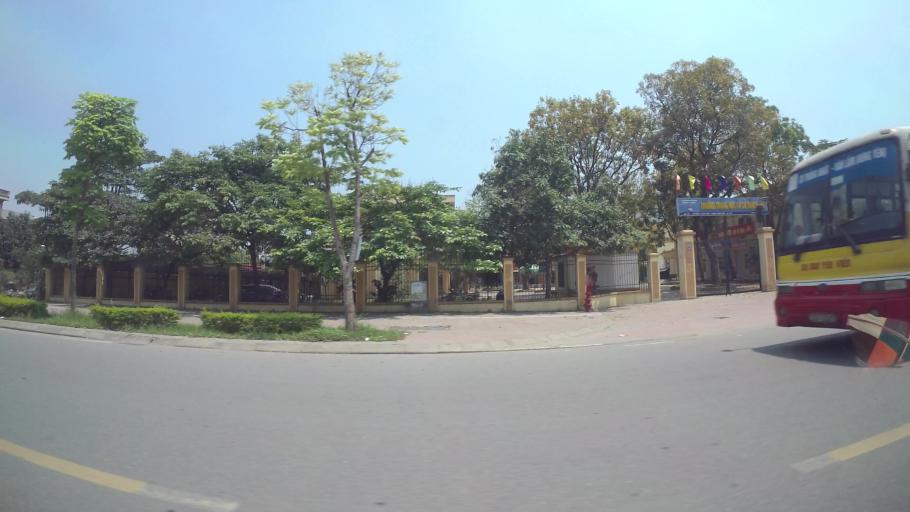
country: VN
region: Ha Noi
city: Trau Quy
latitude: 21.0240
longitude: 105.9064
